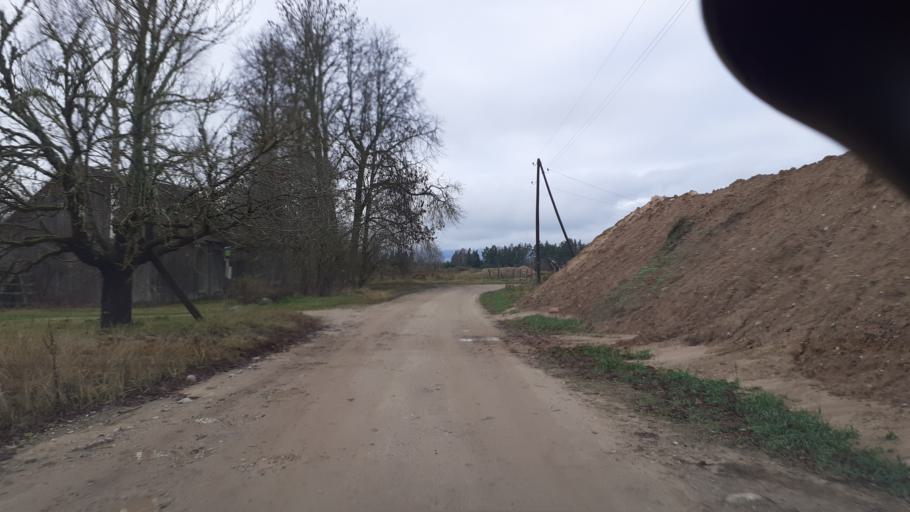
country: LV
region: Kuldigas Rajons
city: Kuldiga
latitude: 57.0452
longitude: 21.8696
